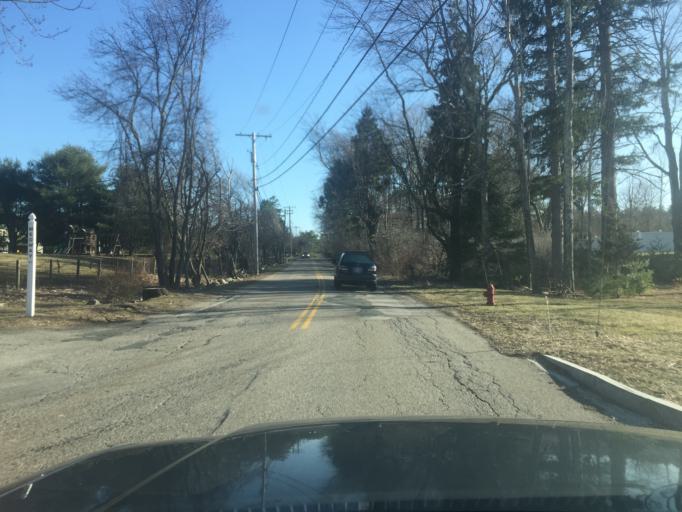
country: US
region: Massachusetts
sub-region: Norfolk County
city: Norfolk
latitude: 42.1276
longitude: -71.3614
